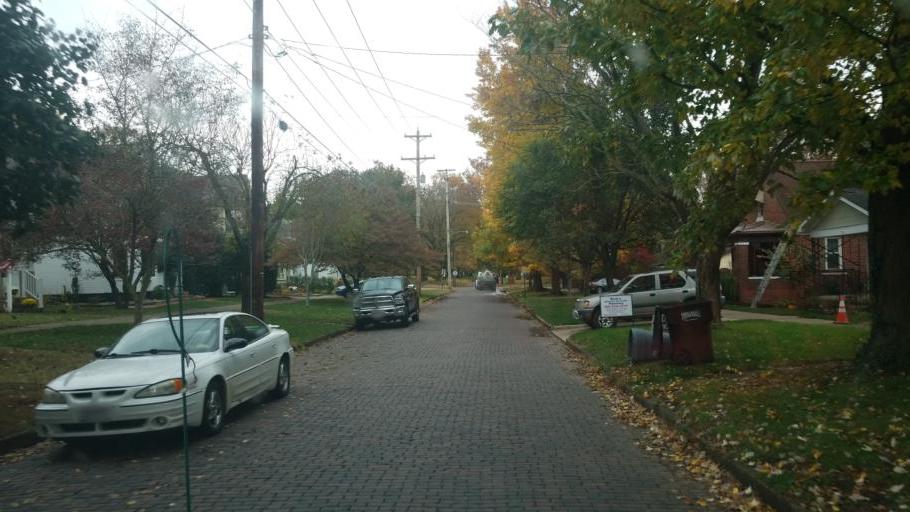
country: US
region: Ohio
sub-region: Washington County
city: Marietta
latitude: 39.4268
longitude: -81.4538
